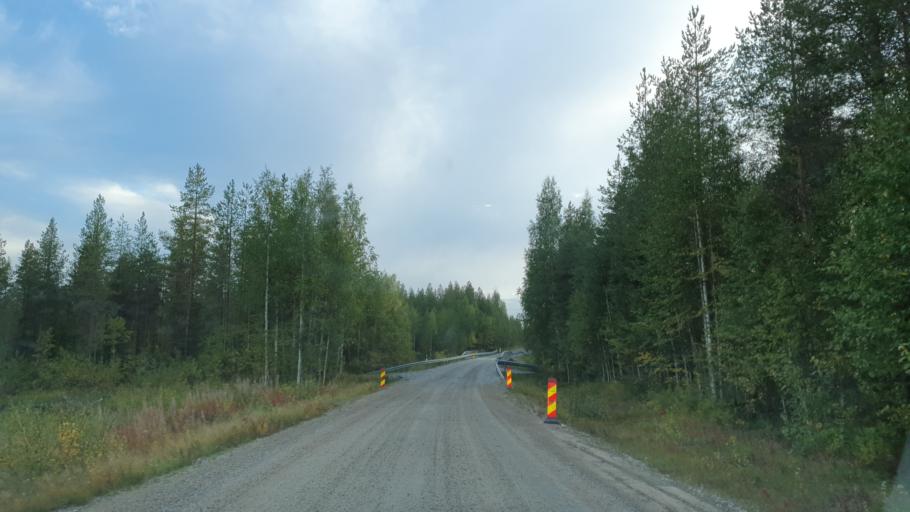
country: FI
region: Kainuu
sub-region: Kehys-Kainuu
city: Kuhmo
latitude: 64.3828
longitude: 29.5564
